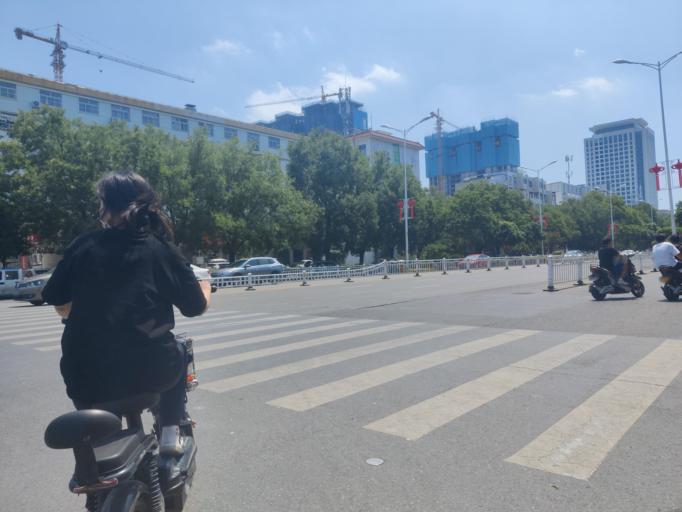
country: CN
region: Henan Sheng
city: Puyang
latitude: 35.7721
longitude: 115.0198
